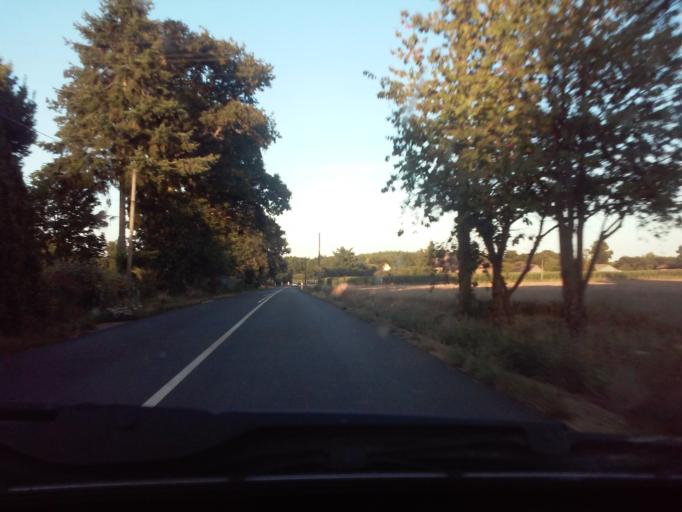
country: FR
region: Brittany
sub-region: Departement d'Ille-et-Vilaine
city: Saint-Pierre-de-Plesguen
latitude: 48.4352
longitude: -1.9392
